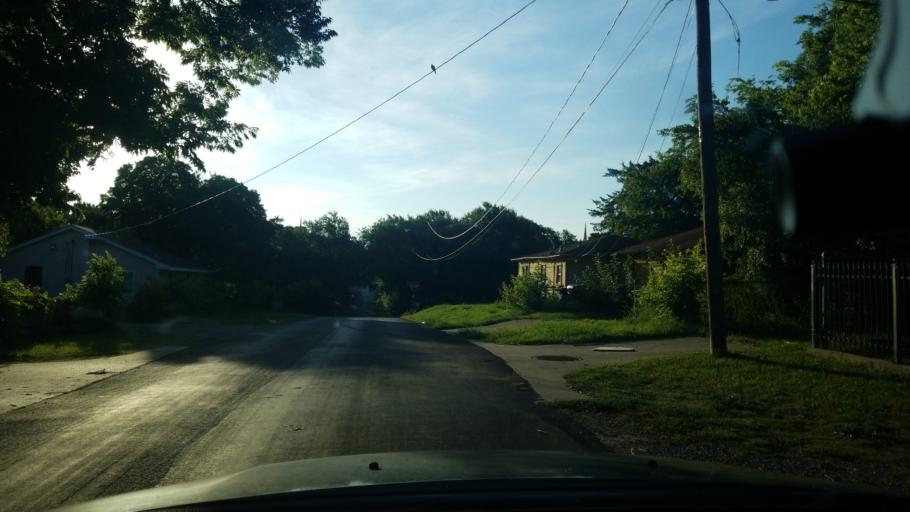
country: US
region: Texas
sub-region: Dallas County
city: Dallas
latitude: 32.7179
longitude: -96.8190
